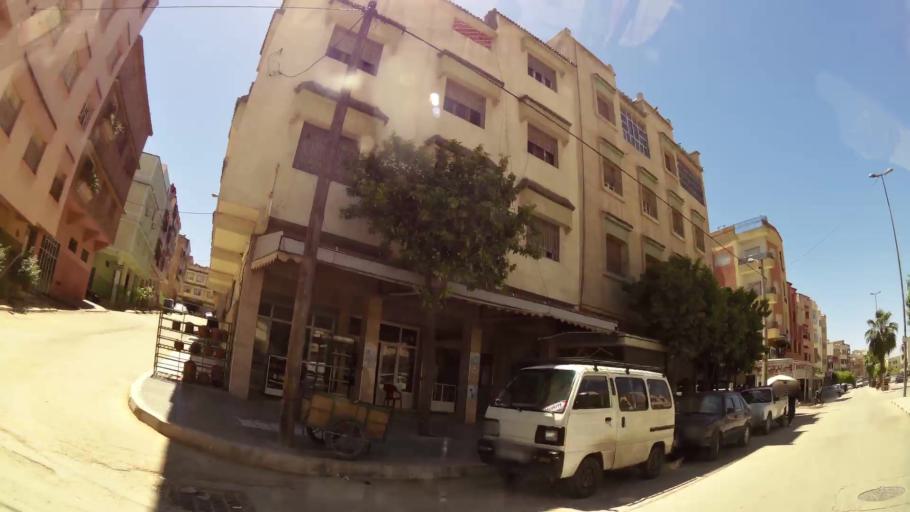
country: MA
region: Meknes-Tafilalet
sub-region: Meknes
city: Meknes
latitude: 33.8986
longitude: -5.5779
